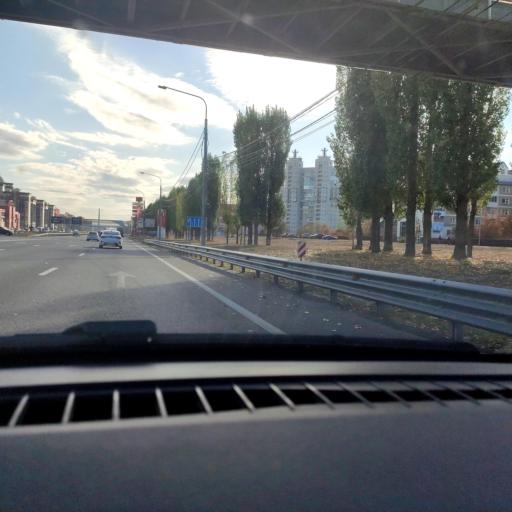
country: RU
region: Voronezj
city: Podgornoye
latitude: 51.7224
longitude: 39.1813
